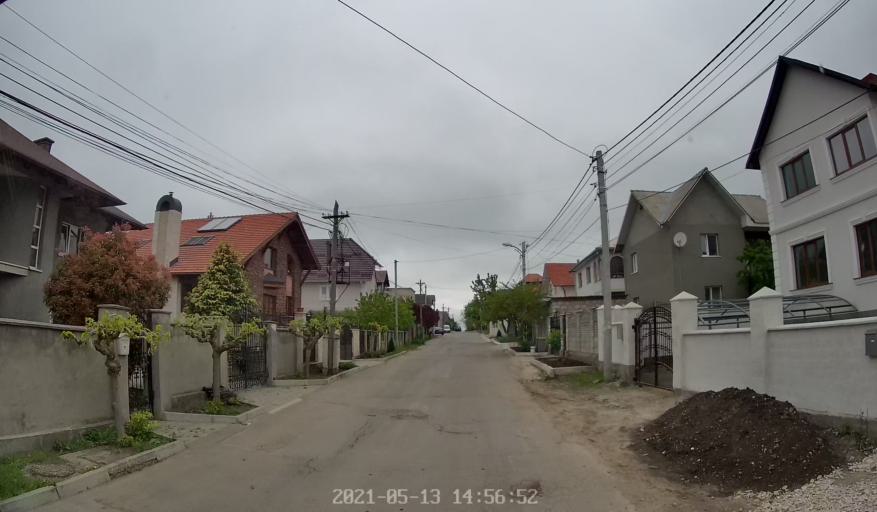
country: MD
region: Chisinau
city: Stauceni
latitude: 47.0990
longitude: 28.8711
